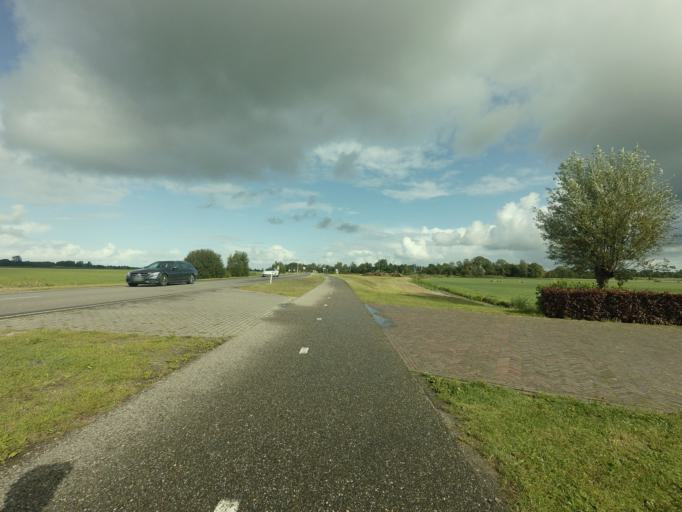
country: NL
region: Friesland
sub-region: Gemeente Tytsjerksteradiel
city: Garyp
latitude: 53.1567
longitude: 5.9511
